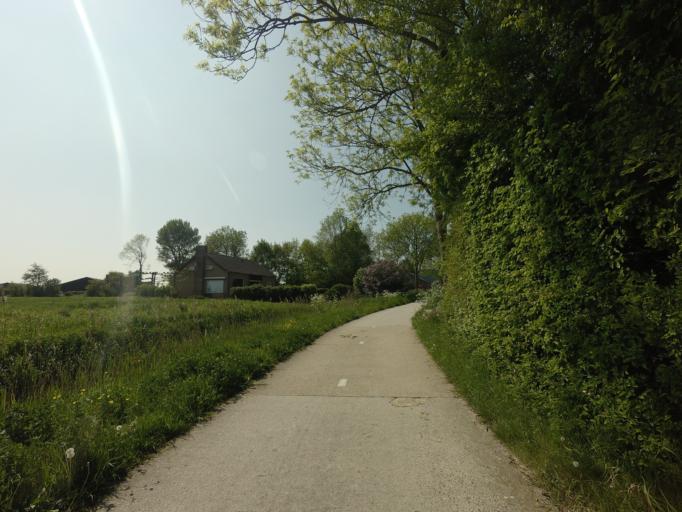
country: NL
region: Zeeland
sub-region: Gemeente Middelburg
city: Middelburg
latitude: 51.5432
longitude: 3.6171
